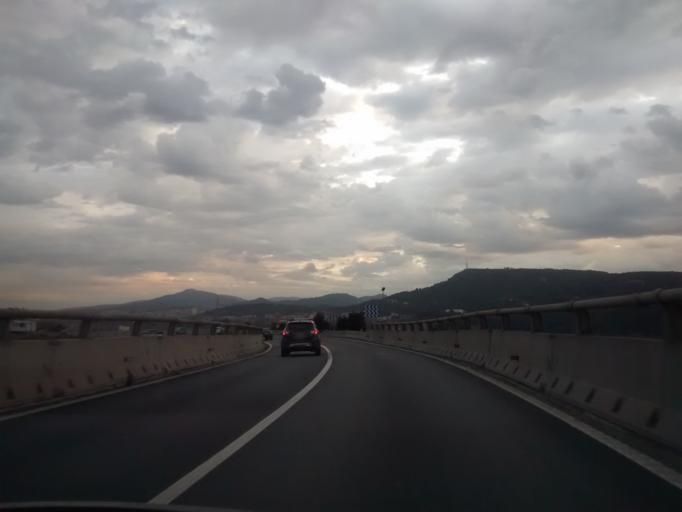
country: ES
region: Catalonia
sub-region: Provincia de Barcelona
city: Palleja
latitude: 41.4416
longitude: 1.9994
